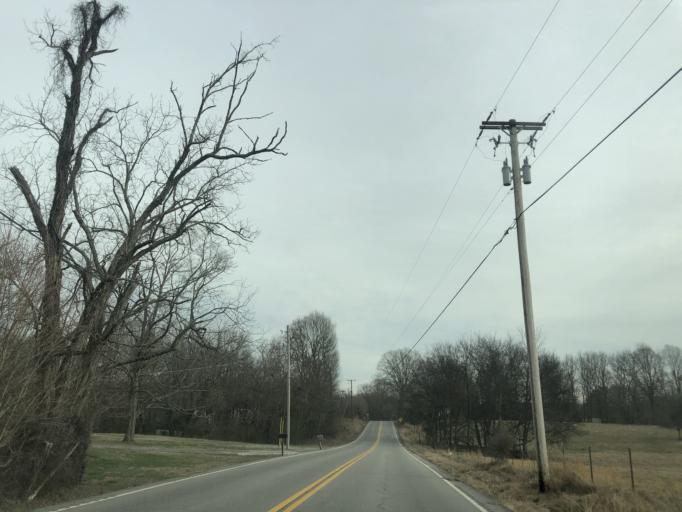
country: US
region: Tennessee
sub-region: Sumner County
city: White House
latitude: 36.4963
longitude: -86.5973
